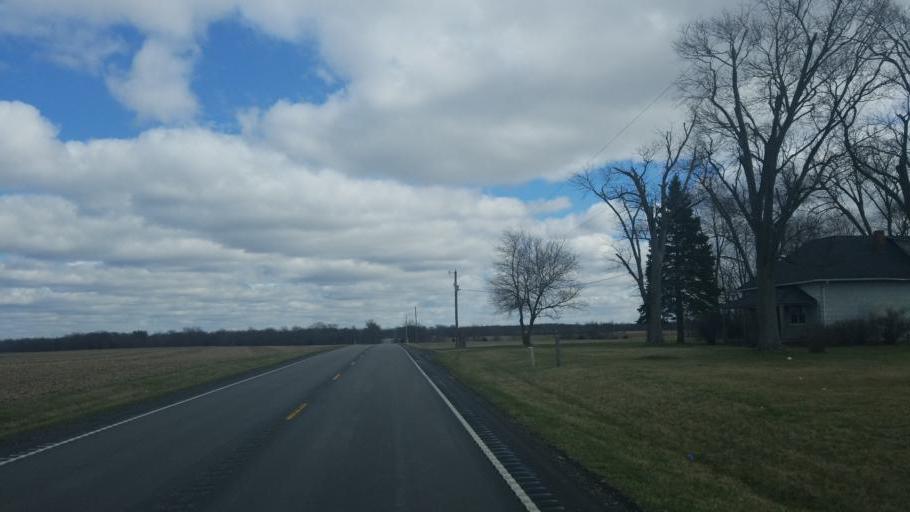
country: US
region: Indiana
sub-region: Parke County
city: Montezuma
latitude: 39.7970
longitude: -87.4620
